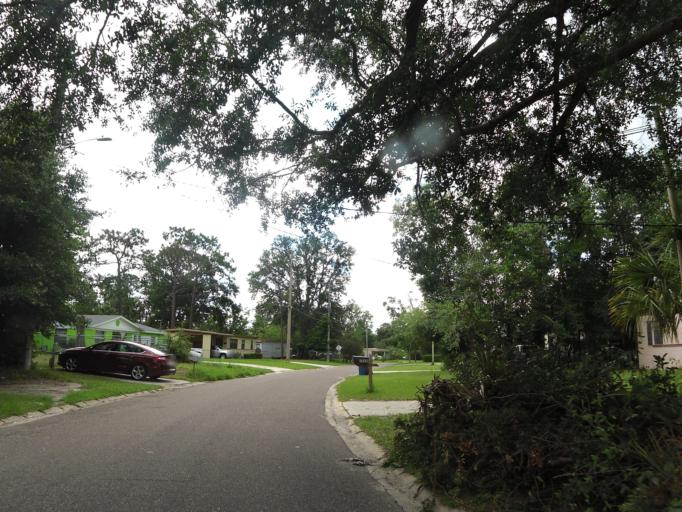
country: US
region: Florida
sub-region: Duval County
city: Jacksonville
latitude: 30.4216
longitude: -81.6675
